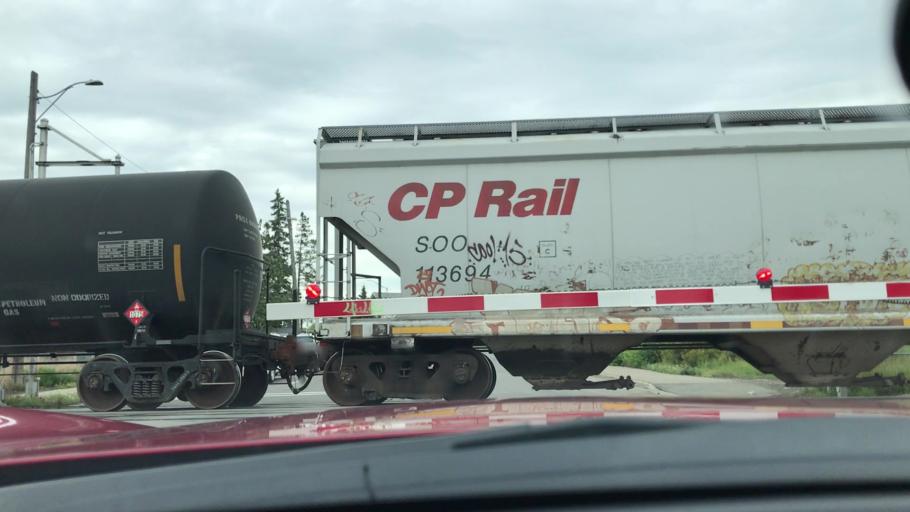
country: CA
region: Alberta
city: Calgary
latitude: 51.0430
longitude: -114.0417
